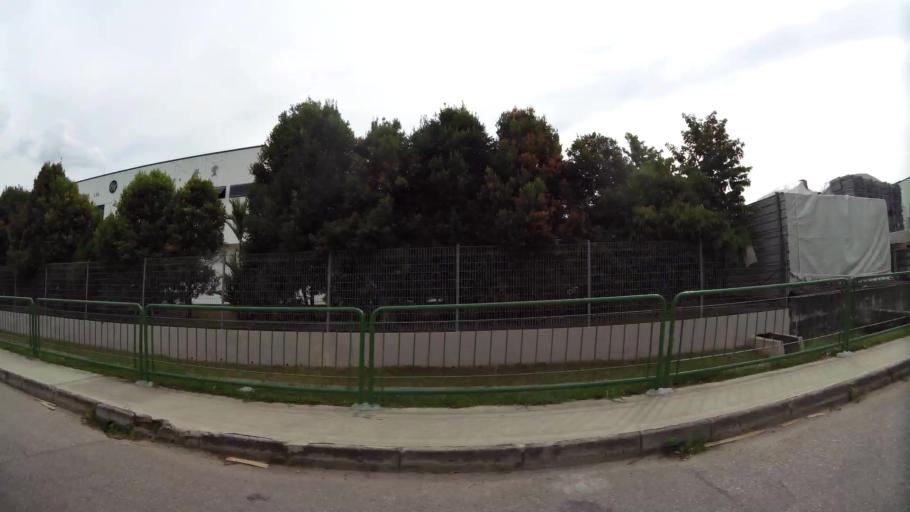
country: MY
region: Johor
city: Johor Bahru
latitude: 1.4378
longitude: 103.7444
